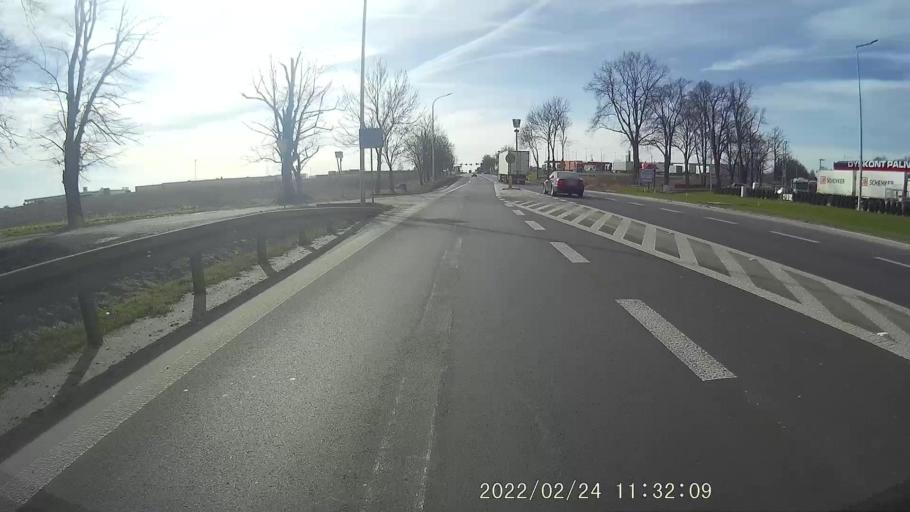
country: PL
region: Lower Silesian Voivodeship
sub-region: Powiat polkowicki
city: Przemkow
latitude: 51.5204
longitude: 15.7433
